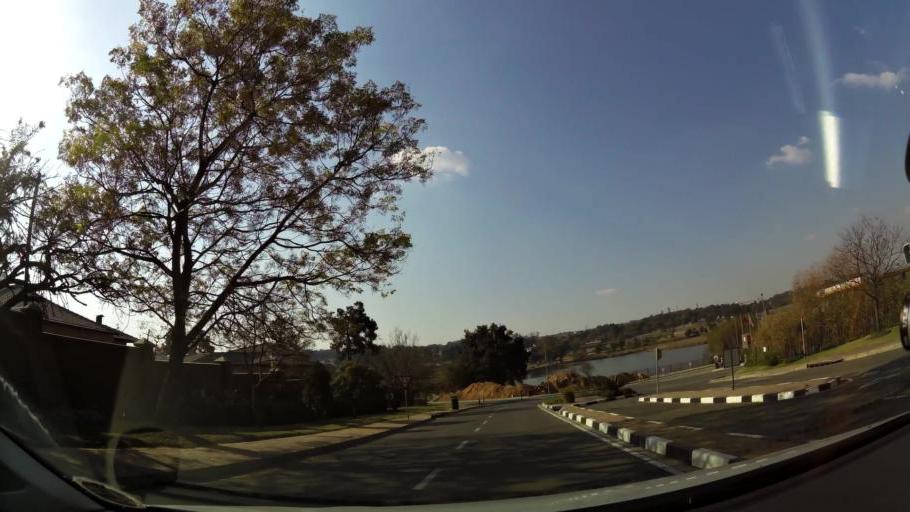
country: ZA
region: Gauteng
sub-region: City of Johannesburg Metropolitan Municipality
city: Modderfontein
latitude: -26.0991
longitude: 28.1505
